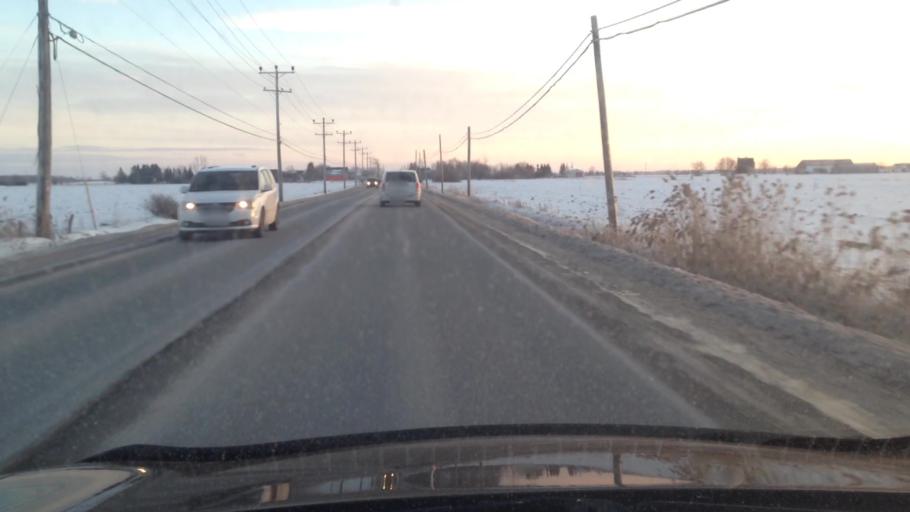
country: CA
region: Quebec
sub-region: Lanaudiere
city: Saint-Lin-Laurentides
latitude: 45.8839
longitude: -73.7579
